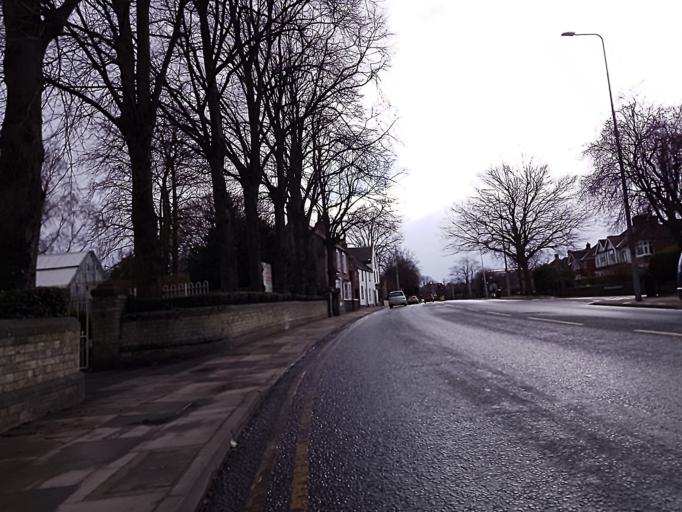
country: GB
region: England
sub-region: North East Lincolnshire
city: Grimbsy
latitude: 53.5586
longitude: -0.0918
